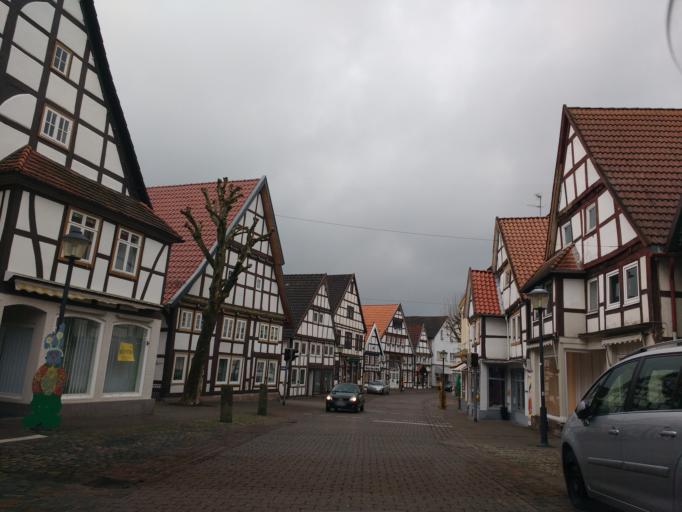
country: DE
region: North Rhine-Westphalia
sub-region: Regierungsbezirk Detmold
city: Blomberg
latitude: 51.9444
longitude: 9.0908
